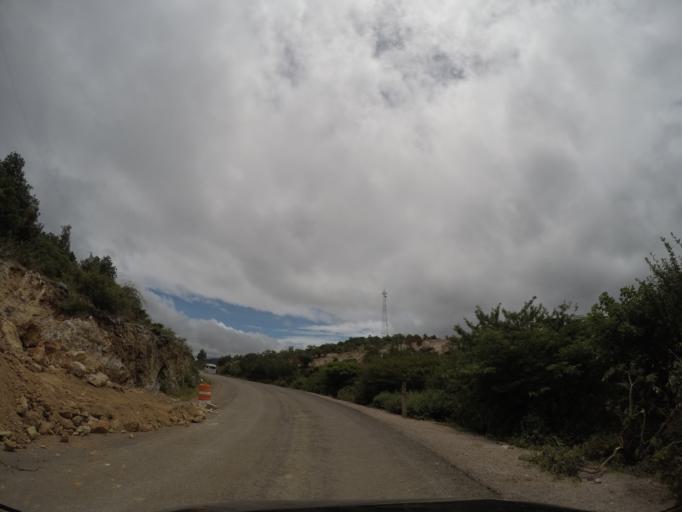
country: MX
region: Oaxaca
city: San Lorenzo Albarradas
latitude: 16.9193
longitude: -96.2563
